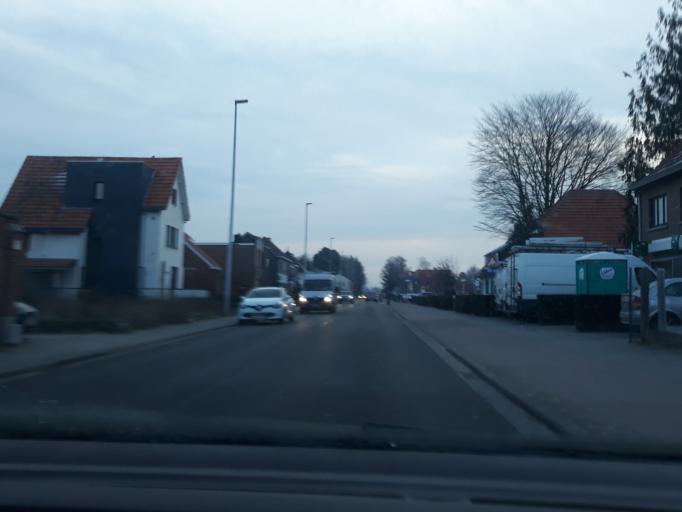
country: BE
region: Flanders
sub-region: Provincie Antwerpen
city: Ravels
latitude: 51.4115
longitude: 5.0033
